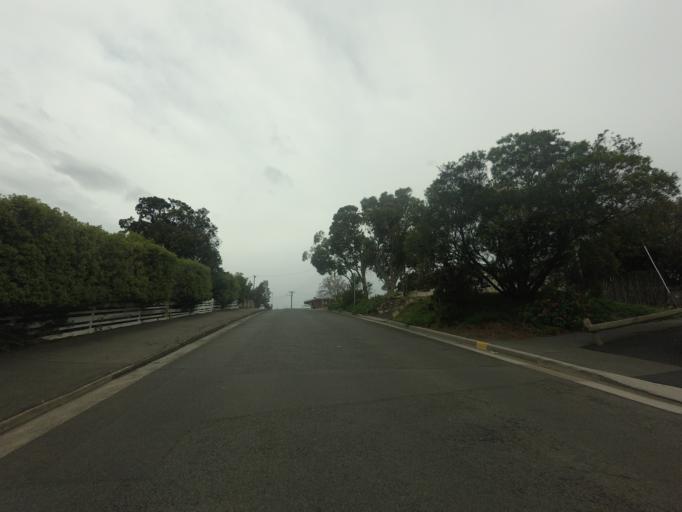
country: AU
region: Tasmania
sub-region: Clarence
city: Bellerive
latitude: -42.8753
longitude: 147.3664
